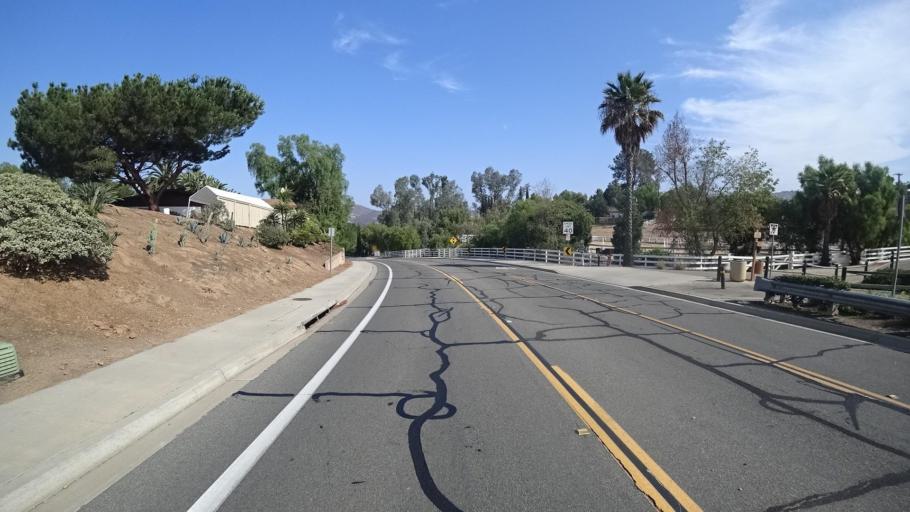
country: US
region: California
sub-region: San Diego County
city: San Marcos
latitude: 33.1646
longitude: -117.1506
